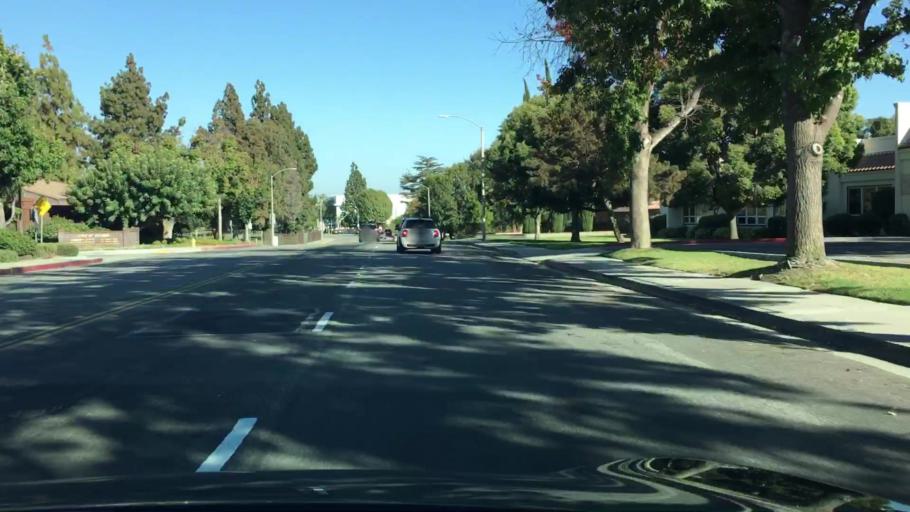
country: US
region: California
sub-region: Los Angeles County
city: Arcadia
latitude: 34.1310
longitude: -118.0447
